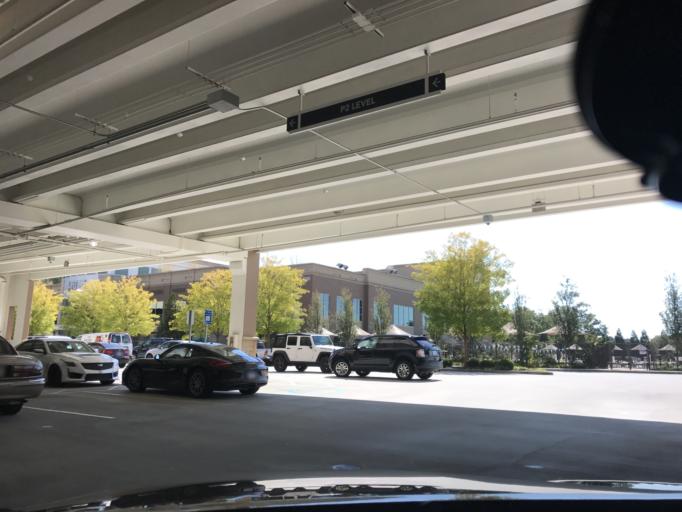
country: US
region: Georgia
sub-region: Fulton County
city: Sandy Springs
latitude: 33.9075
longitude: -84.3806
